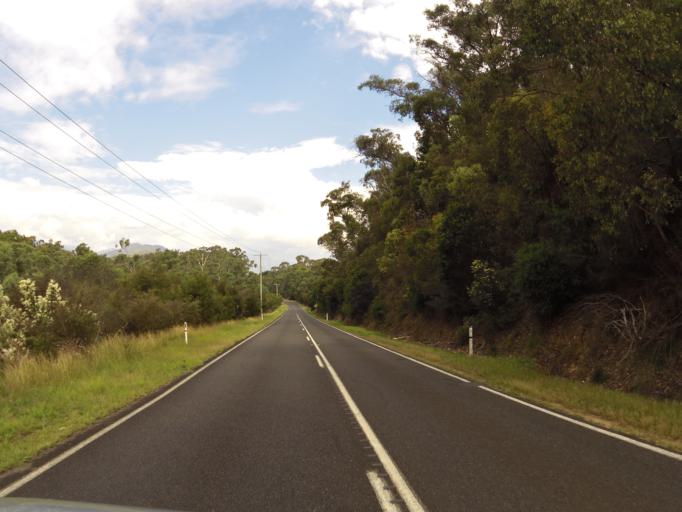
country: AU
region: Victoria
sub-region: Alpine
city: Mount Beauty
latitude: -36.7514
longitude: 147.0175
